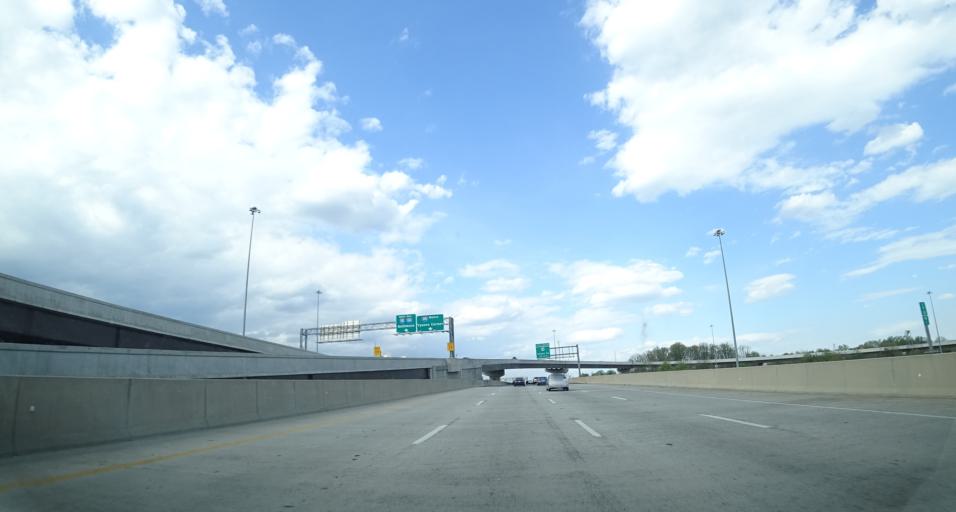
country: US
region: Virginia
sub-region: Fairfax County
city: Springfield
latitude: 38.7912
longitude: -77.1746
